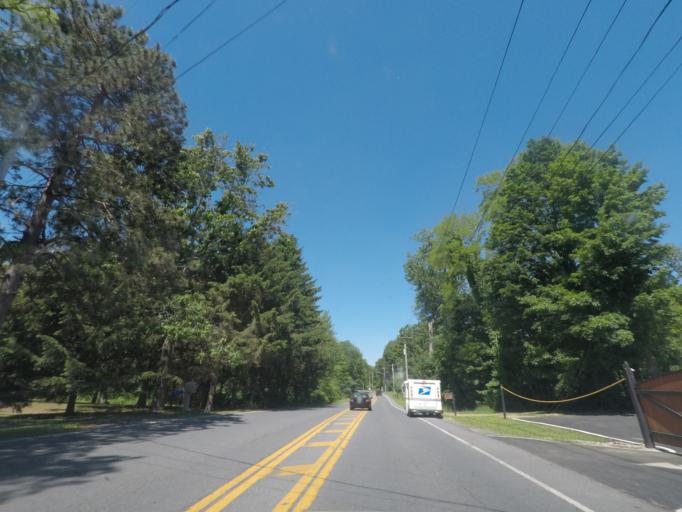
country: US
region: New York
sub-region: Saratoga County
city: Country Knolls
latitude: 42.8552
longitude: -73.7950
